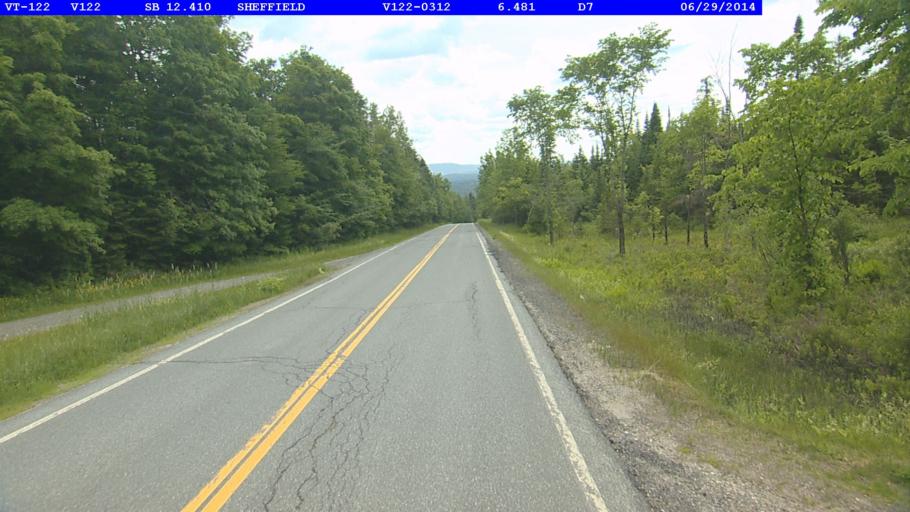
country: US
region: Vermont
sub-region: Caledonia County
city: Lyndonville
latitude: 44.6616
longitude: -72.1619
